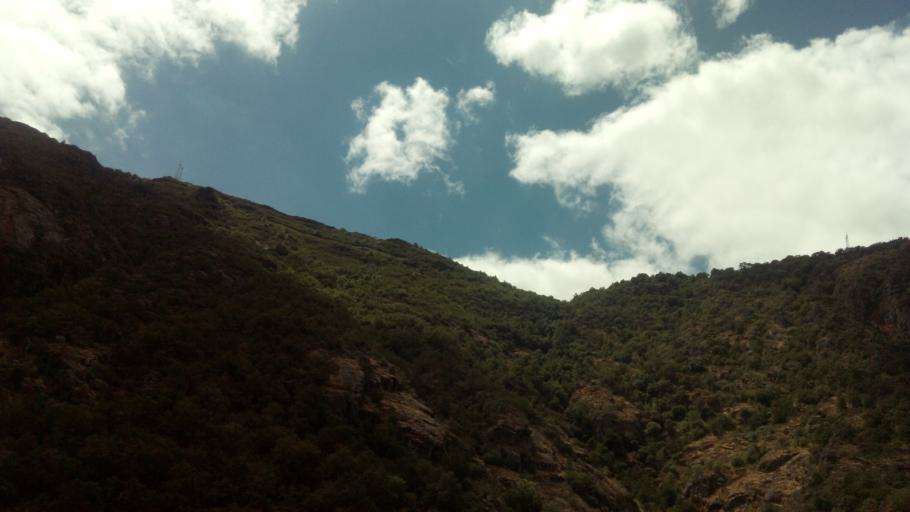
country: ES
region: Galicia
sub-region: Provincia de Lugo
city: Sober
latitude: 42.3846
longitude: -7.6143
